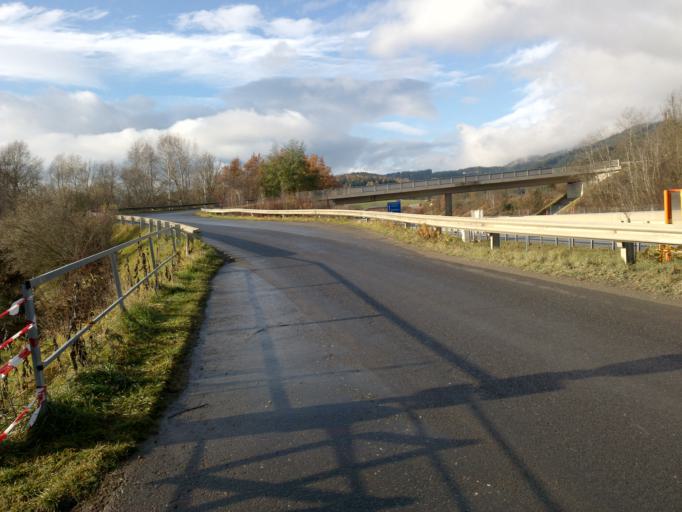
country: AT
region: Styria
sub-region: Politischer Bezirk Murtal
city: Kobenz
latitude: 47.2385
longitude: 14.8447
